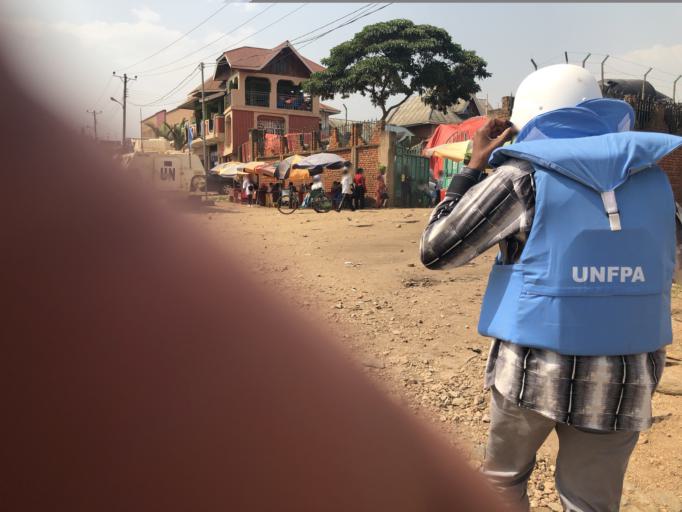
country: UG
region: Western Region
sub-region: Kasese District
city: Kilembe
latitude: 0.0395
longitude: 29.7186
